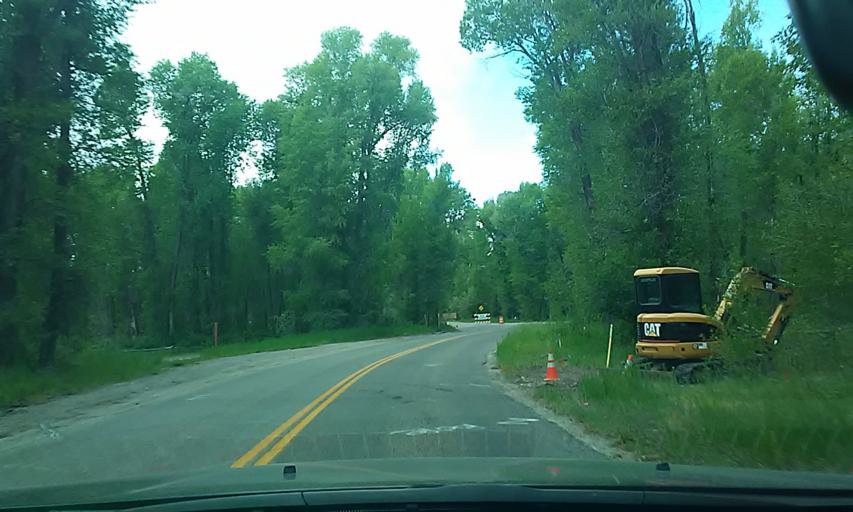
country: US
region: Wyoming
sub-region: Teton County
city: Jackson
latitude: 43.5597
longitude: -110.7614
